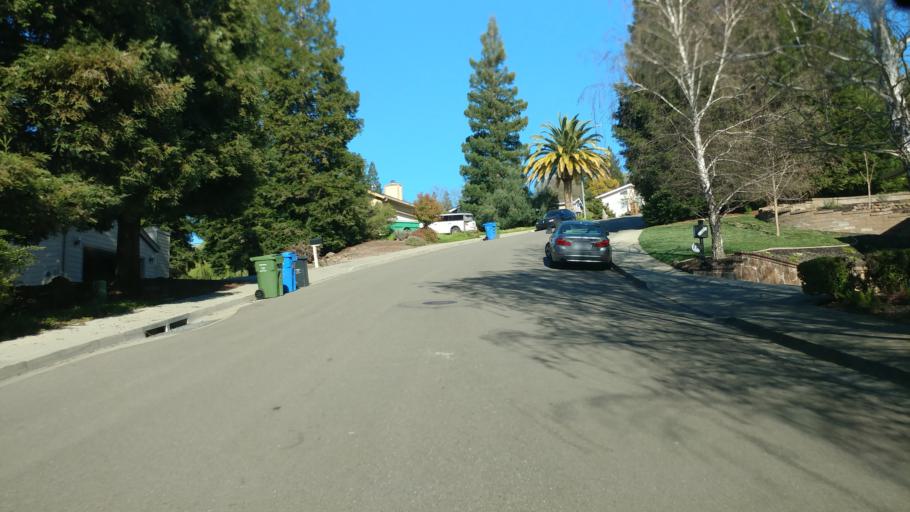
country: US
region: California
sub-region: Contra Costa County
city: San Ramon
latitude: 37.8065
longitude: -121.9750
